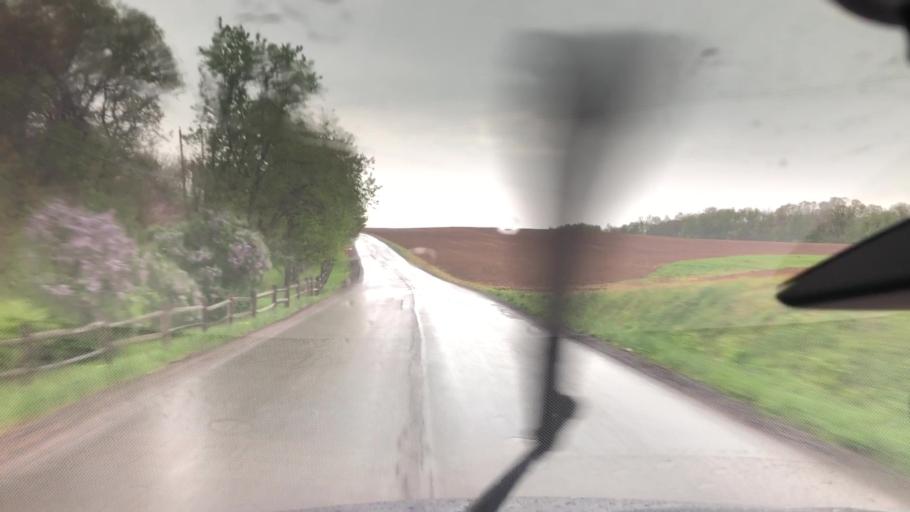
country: US
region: Pennsylvania
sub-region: Butler County
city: Saxonburg
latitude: 40.7516
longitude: -79.8571
